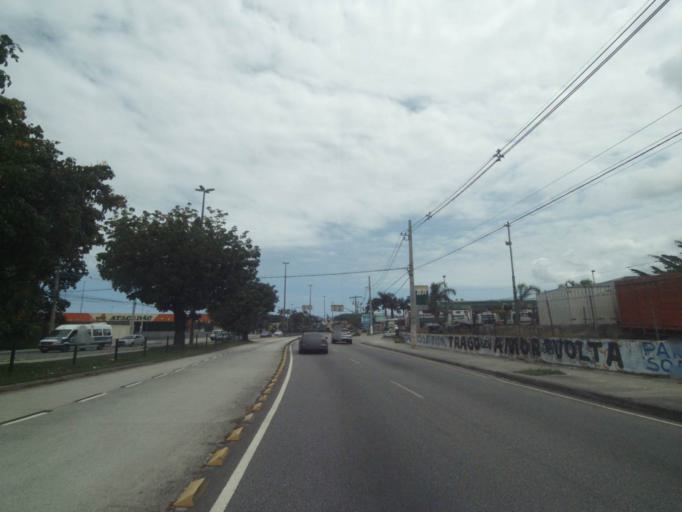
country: BR
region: Rio de Janeiro
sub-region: Sao Joao De Meriti
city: Sao Joao de Meriti
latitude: -22.9526
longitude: -43.3750
